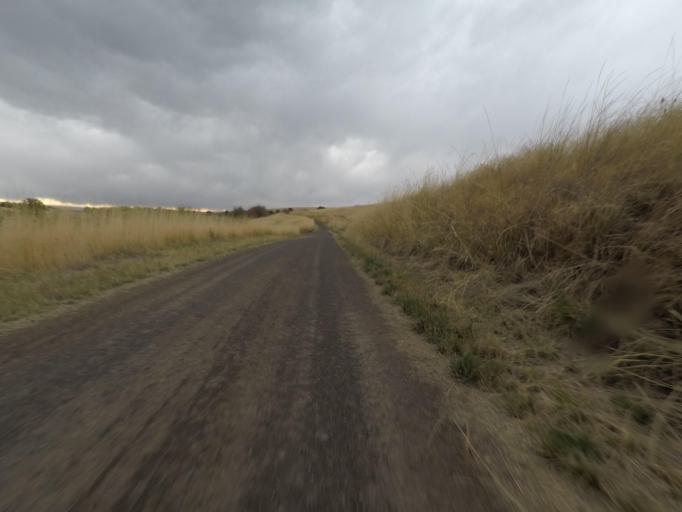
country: US
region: Washington
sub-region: Walla Walla County
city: Walla Walla East
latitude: 46.0764
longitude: -118.2569
